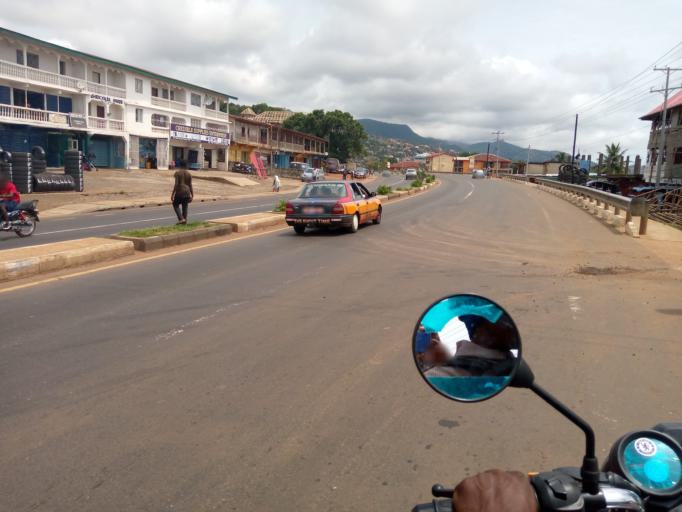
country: SL
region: Western Area
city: Hastings
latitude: 8.4123
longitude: -13.1442
